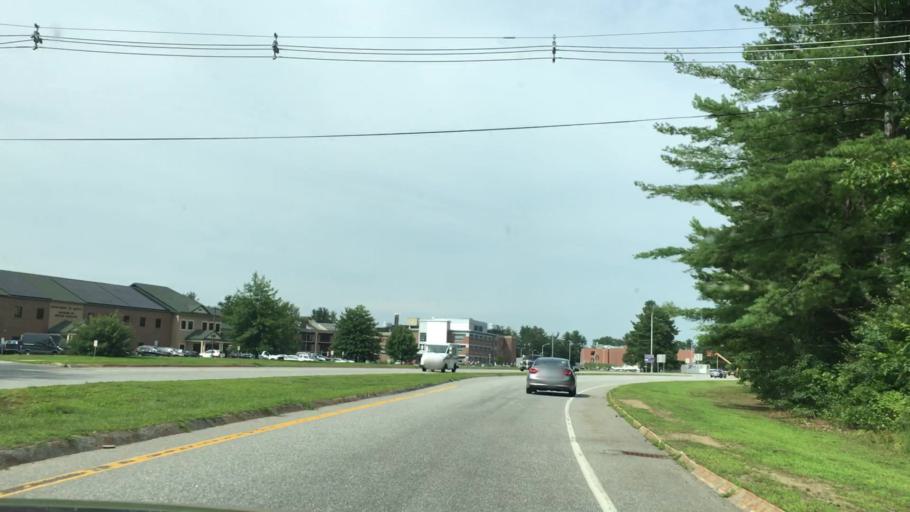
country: US
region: New Hampshire
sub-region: Merrimack County
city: Concord
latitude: 43.2165
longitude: -71.5170
